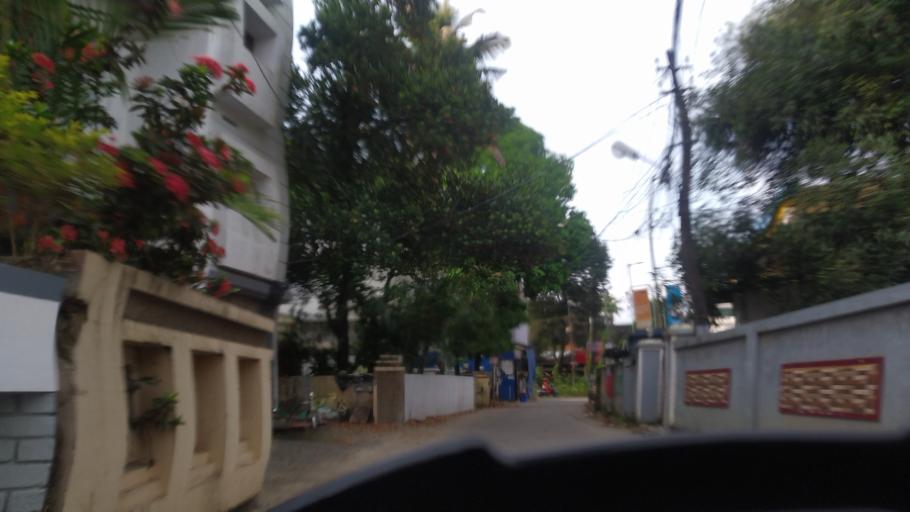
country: IN
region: Kerala
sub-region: Ernakulam
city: Cochin
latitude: 9.9853
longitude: 76.3090
